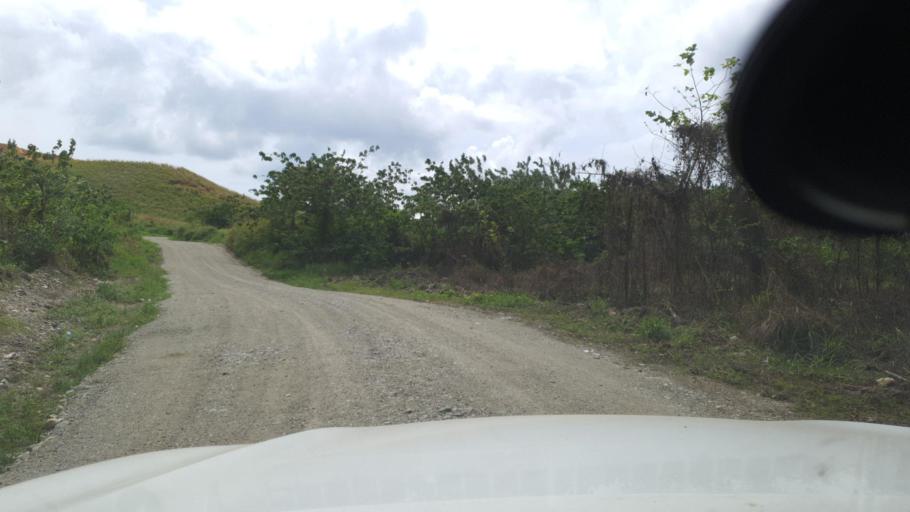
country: SB
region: Guadalcanal
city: Honiara
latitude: -9.4187
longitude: 159.8872
